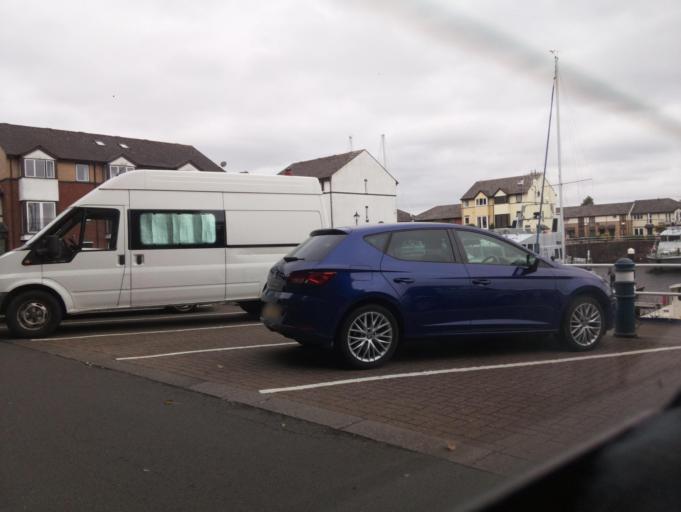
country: GB
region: Wales
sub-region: Vale of Glamorgan
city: Penarth
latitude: 51.4450
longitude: -3.1705
